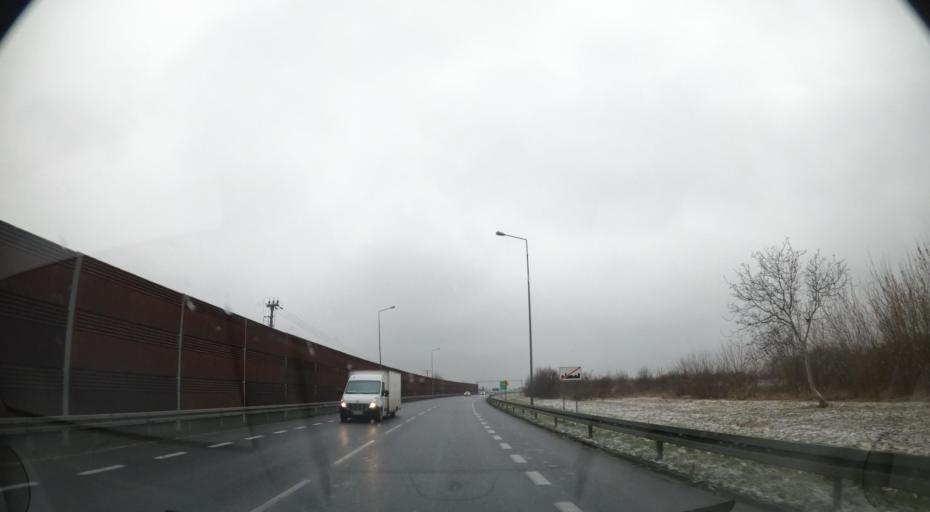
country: PL
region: Masovian Voivodeship
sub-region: Powiat sochaczewski
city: Sochaczew
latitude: 52.2090
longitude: 20.2495
